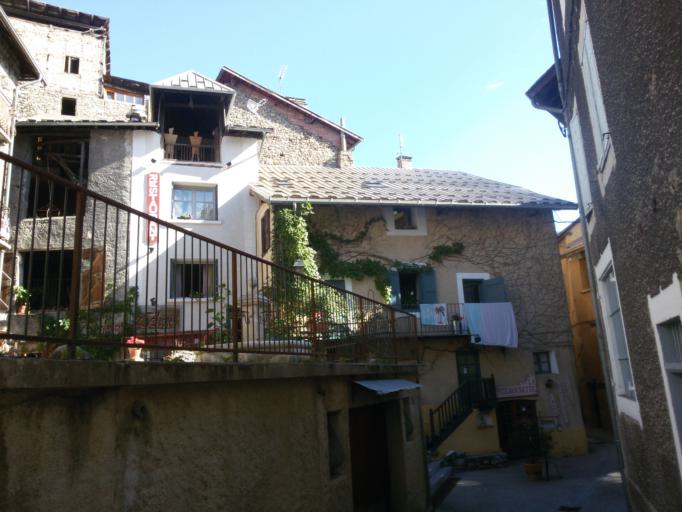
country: FR
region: Provence-Alpes-Cote d'Azur
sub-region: Departement des Hautes-Alpes
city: Guillestre
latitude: 44.6598
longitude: 6.6488
